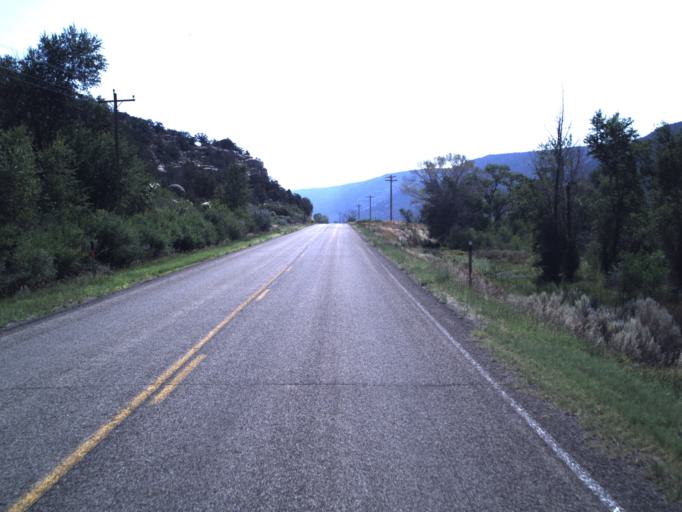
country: US
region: Utah
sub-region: Duchesne County
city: Duchesne
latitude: 40.3046
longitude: -110.6249
